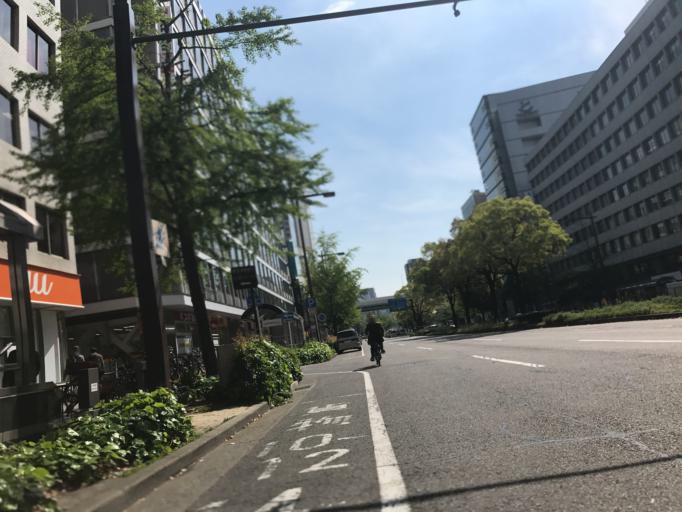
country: JP
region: Aichi
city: Nagoya-shi
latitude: 35.1719
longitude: 136.8874
